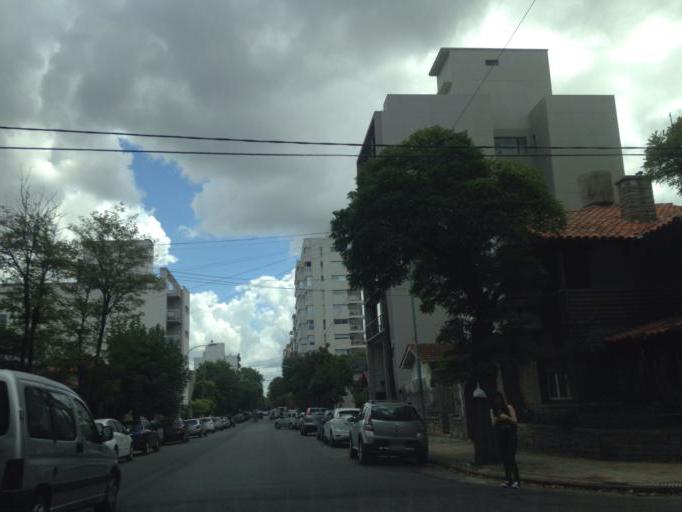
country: AR
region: Buenos Aires
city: Mar del Plata
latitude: -38.0091
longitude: -57.5501
